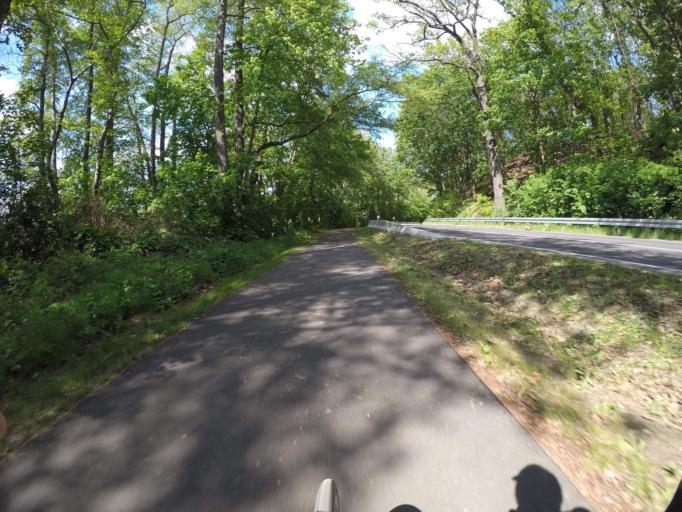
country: DE
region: Brandenburg
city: Potsdam
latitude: 52.3737
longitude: 13.0372
